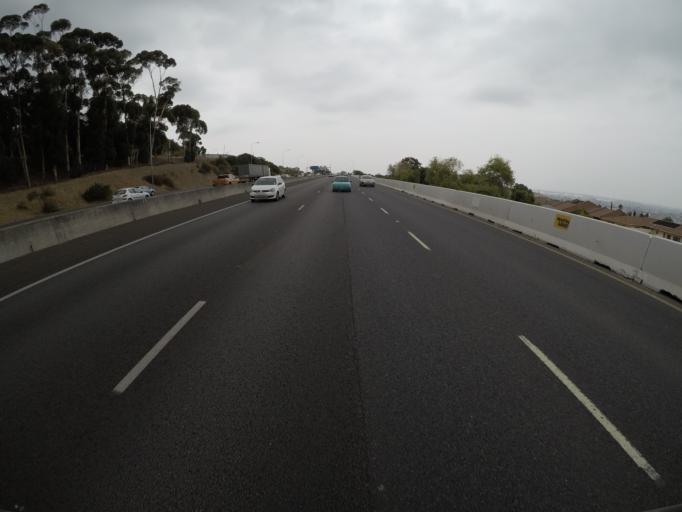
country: ZA
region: Western Cape
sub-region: City of Cape Town
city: Sunset Beach
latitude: -33.8867
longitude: 18.5960
